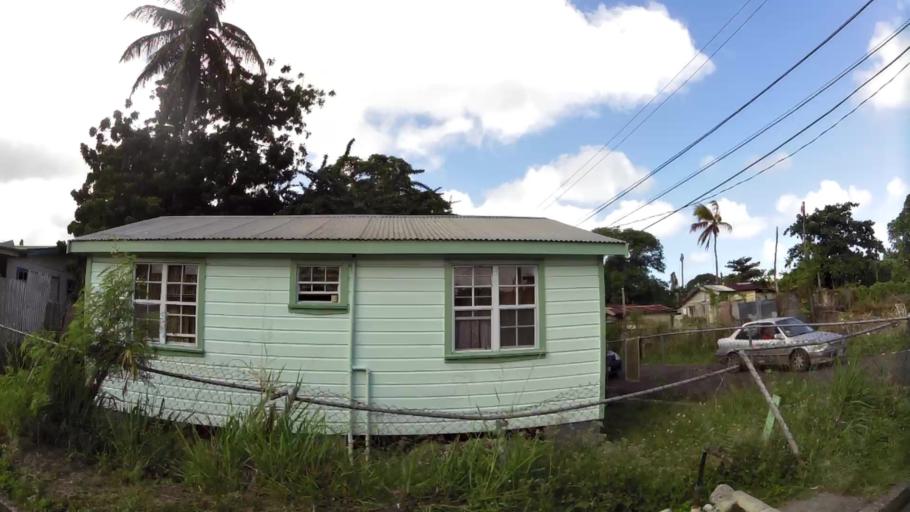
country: AG
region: Saint John
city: Saint John's
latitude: 17.1124
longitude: -61.8373
